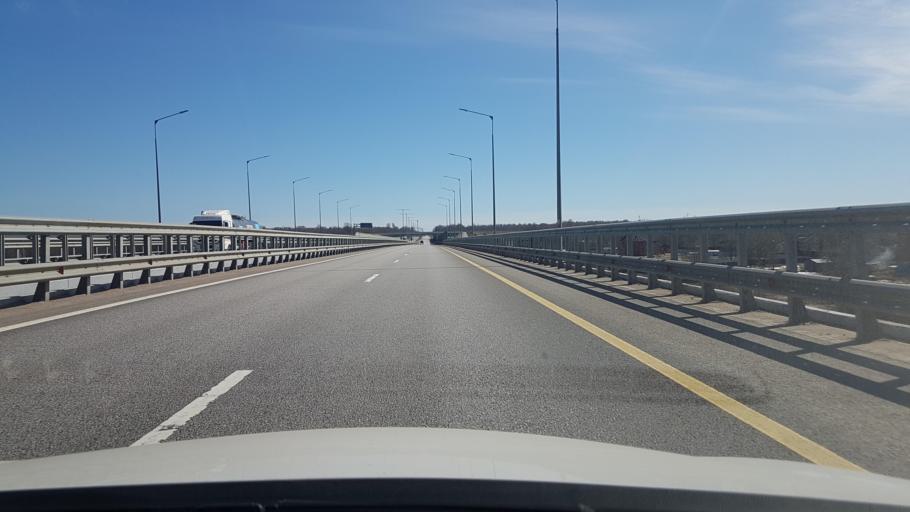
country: RU
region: Novgorod
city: Krechevitsy
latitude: 58.7394
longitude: 31.5304
